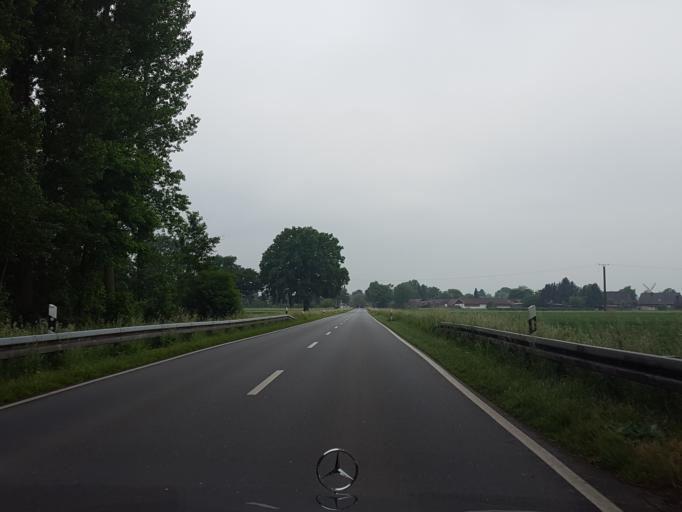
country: DE
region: North Rhine-Westphalia
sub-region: Regierungsbezirk Munster
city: Senden
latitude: 51.8239
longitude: 7.5606
